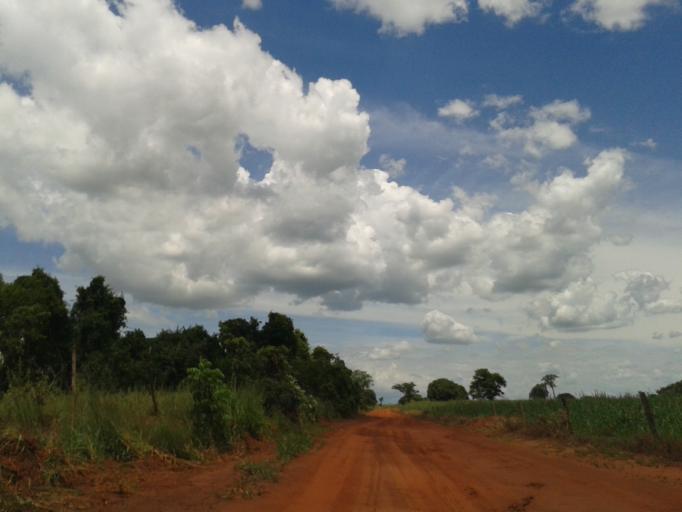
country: BR
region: Minas Gerais
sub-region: Ituiutaba
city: Ituiutaba
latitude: -18.8728
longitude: -49.4843
